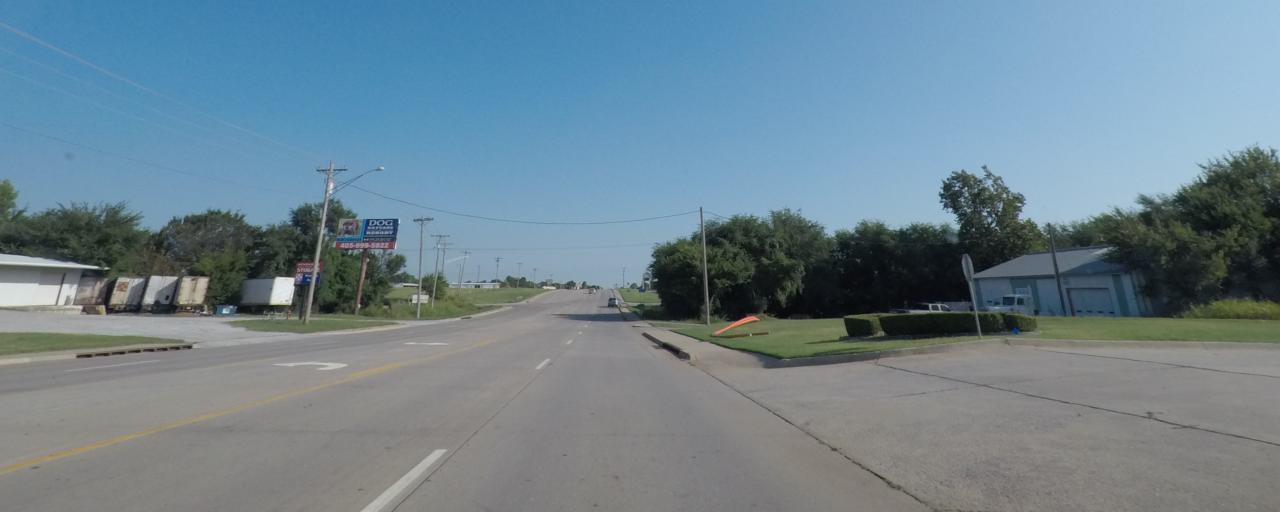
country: US
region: Oklahoma
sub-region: McClain County
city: Newcastle
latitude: 35.2607
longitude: -97.6001
